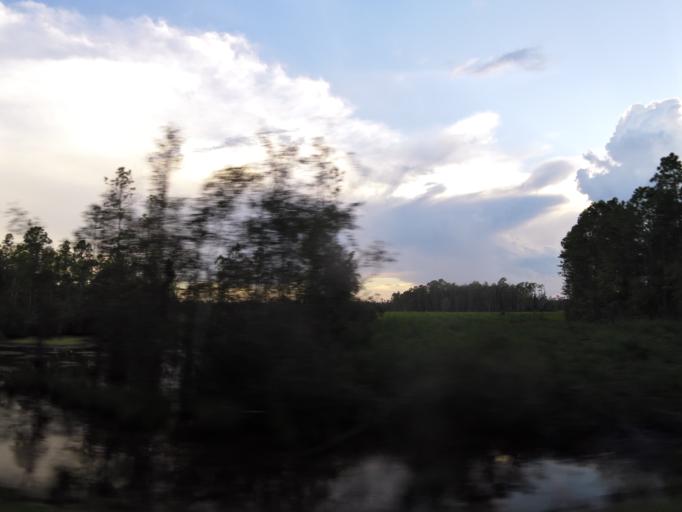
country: US
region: Georgia
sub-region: Echols County
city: Statenville
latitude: 30.7469
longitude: -83.1054
